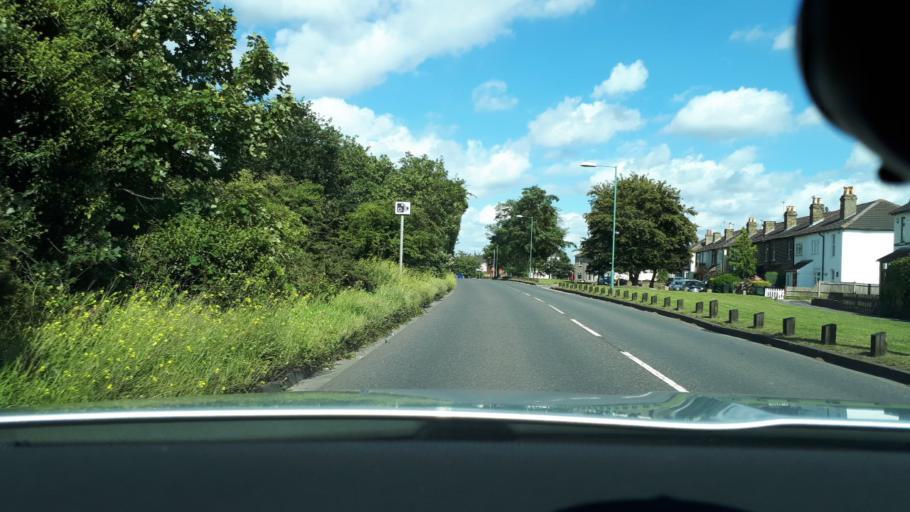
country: GB
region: England
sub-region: Kent
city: Swanley
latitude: 51.4312
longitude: 0.1842
